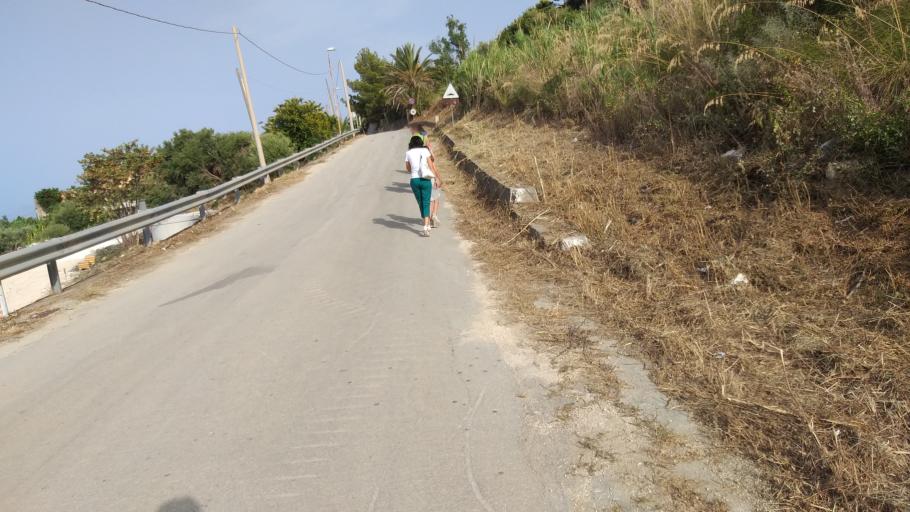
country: IT
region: Sicily
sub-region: Trapani
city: Castelluzzo
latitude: 38.0717
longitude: 12.8148
